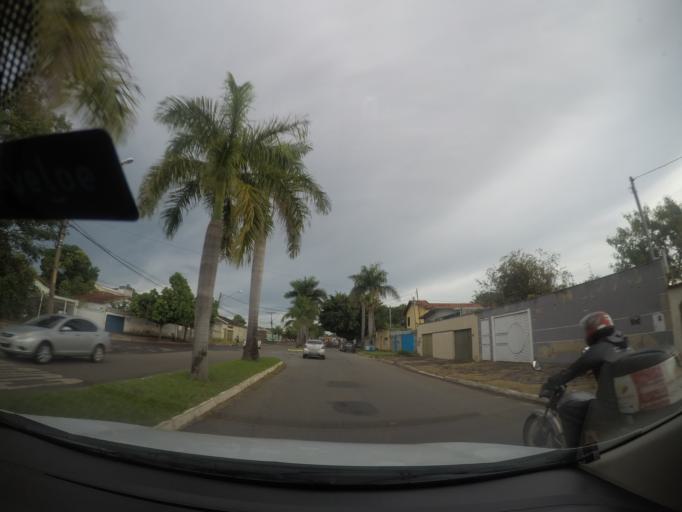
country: BR
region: Goias
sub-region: Goiania
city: Goiania
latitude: -16.7184
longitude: -49.3104
